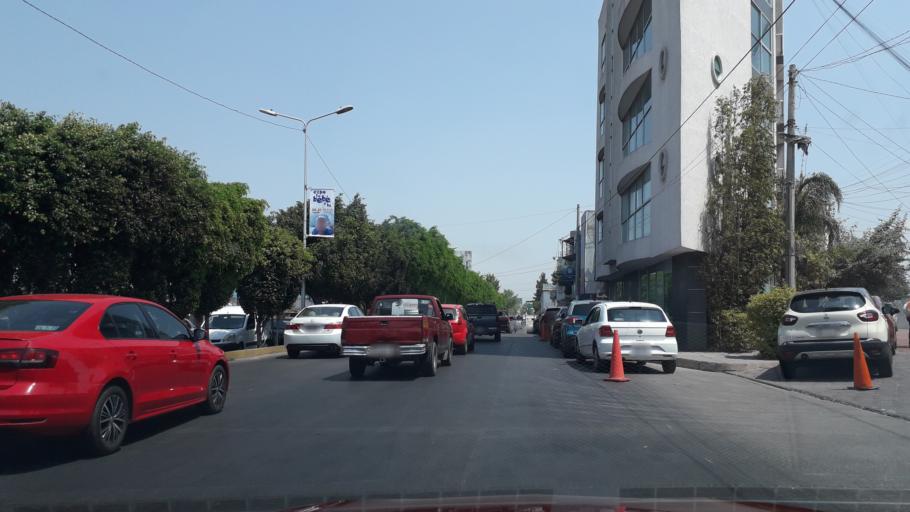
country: MX
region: Puebla
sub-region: San Pedro Cholula
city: Santiago Momoxpan
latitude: 19.0525
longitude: -98.2380
